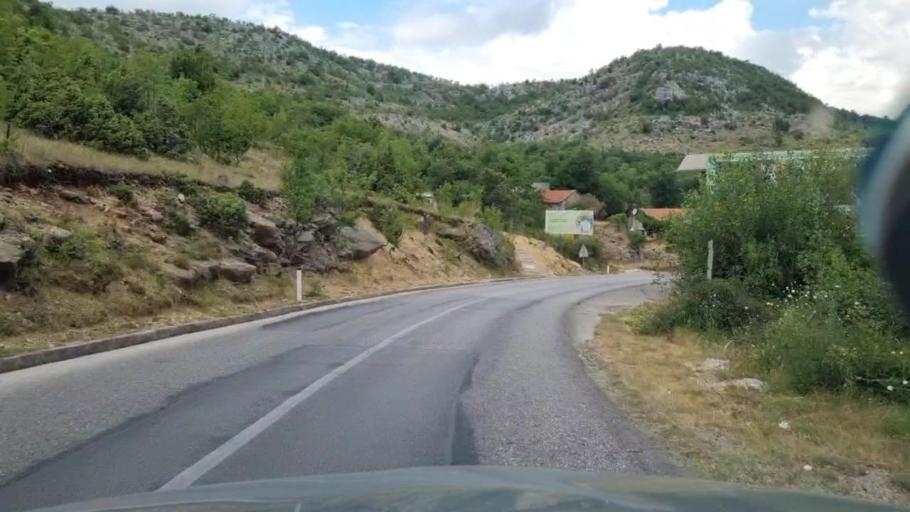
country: BA
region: Federation of Bosnia and Herzegovina
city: Rodoc
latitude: 43.3247
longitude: 17.7917
